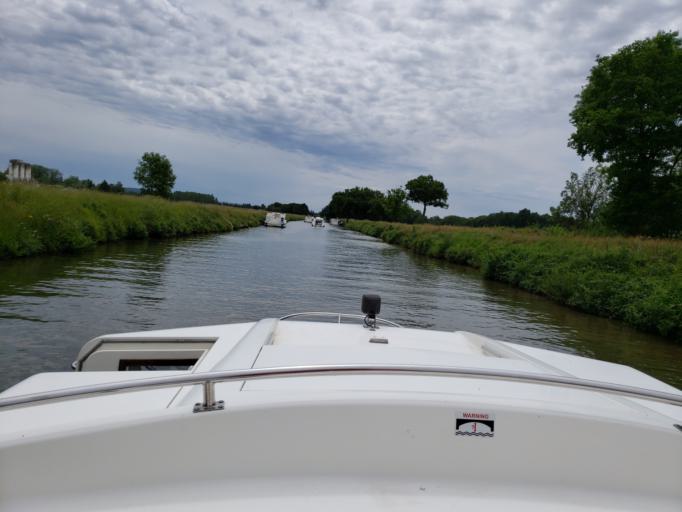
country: FR
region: Bourgogne
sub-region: Departement de l'Yonne
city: Gurgy
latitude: 47.8793
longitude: 3.5490
